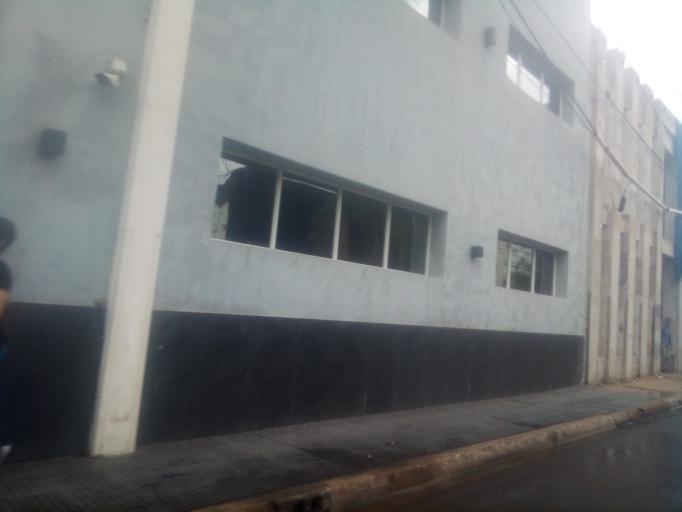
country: AR
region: Corrientes
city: Corrientes
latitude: -27.4656
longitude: -58.8335
